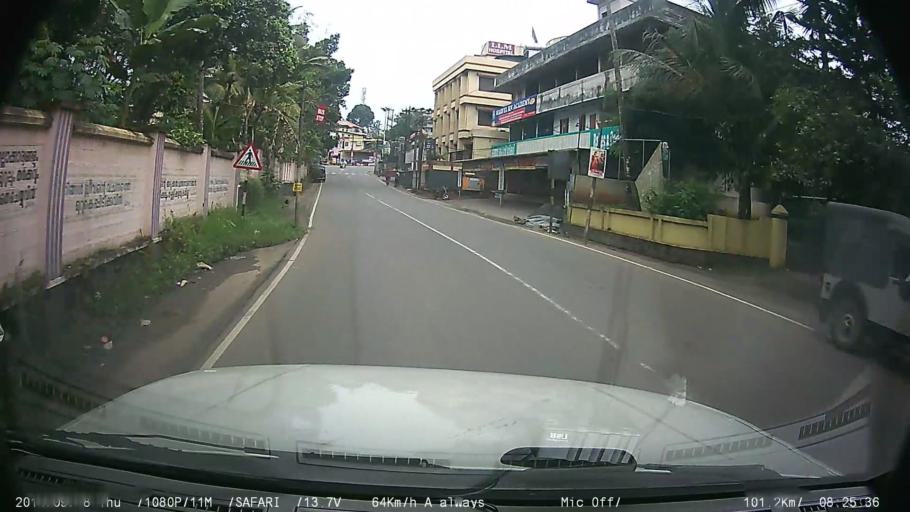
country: IN
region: Kerala
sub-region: Kottayam
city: Palackattumala
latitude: 9.6826
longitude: 76.6114
